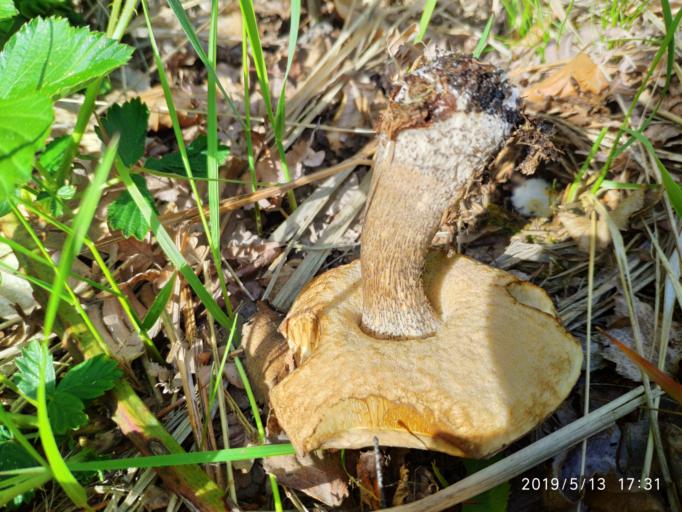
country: PL
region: Lubusz
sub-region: Powiat zielonogorski
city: Czerwiensk
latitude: 51.9987
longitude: 15.4440
